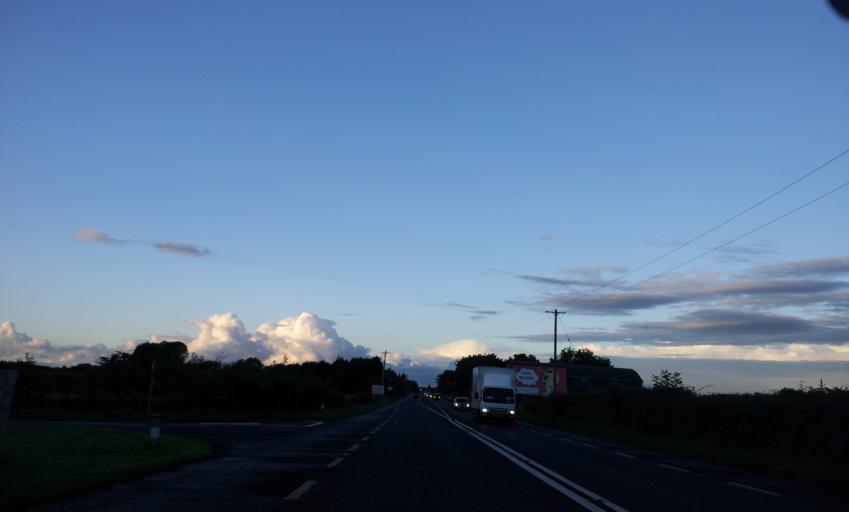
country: IE
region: Munster
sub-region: County Limerick
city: Newcastle West
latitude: 52.4620
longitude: -9.0297
